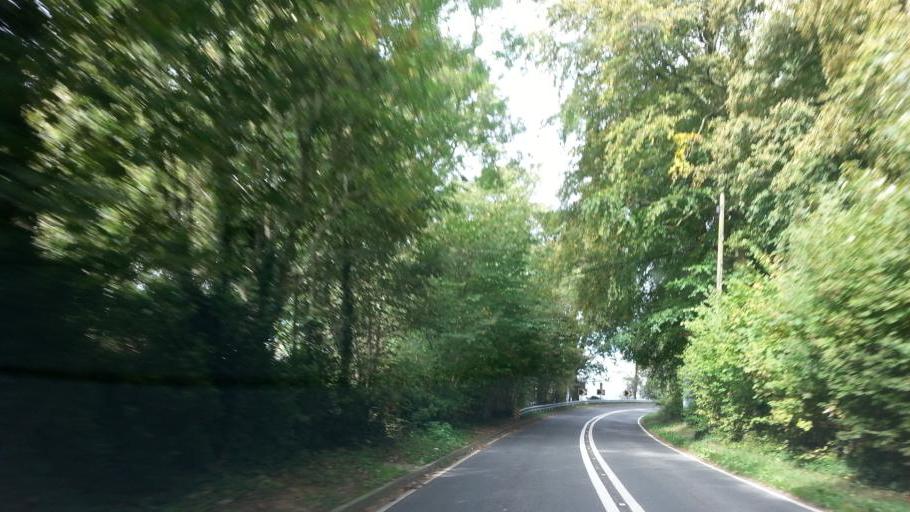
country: GB
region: England
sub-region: Gloucestershire
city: Painswick
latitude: 51.8228
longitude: -2.1702
